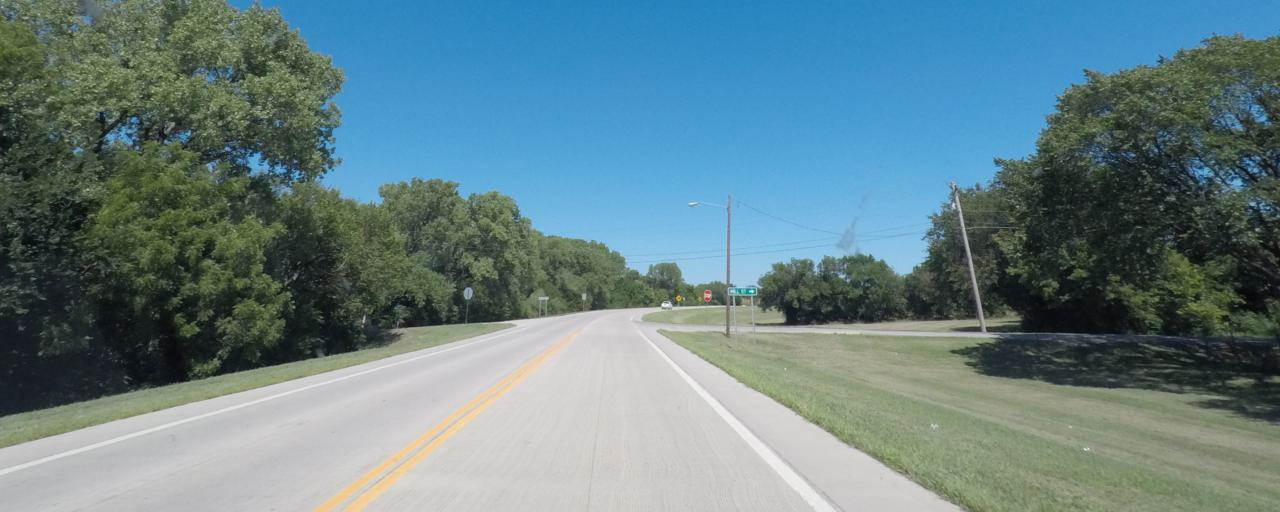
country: US
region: Kansas
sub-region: Sumner County
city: Wellington
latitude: 37.2570
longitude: -97.4060
